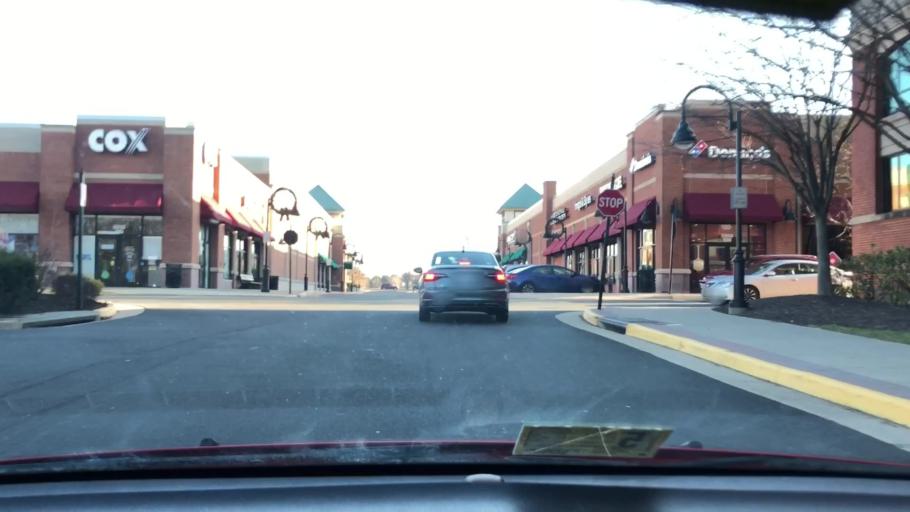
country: US
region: Virginia
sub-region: Fairfax County
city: Franconia
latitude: 38.7710
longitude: -77.1411
